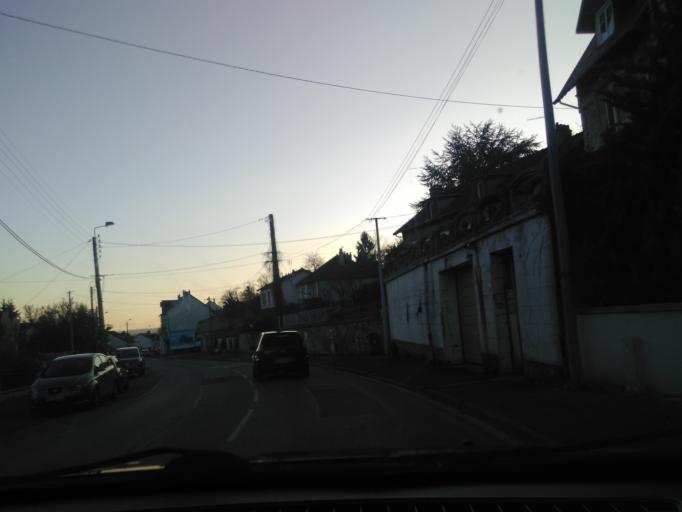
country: FR
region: Picardie
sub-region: Departement de l'Aisne
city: Laon
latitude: 49.5616
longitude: 3.6323
